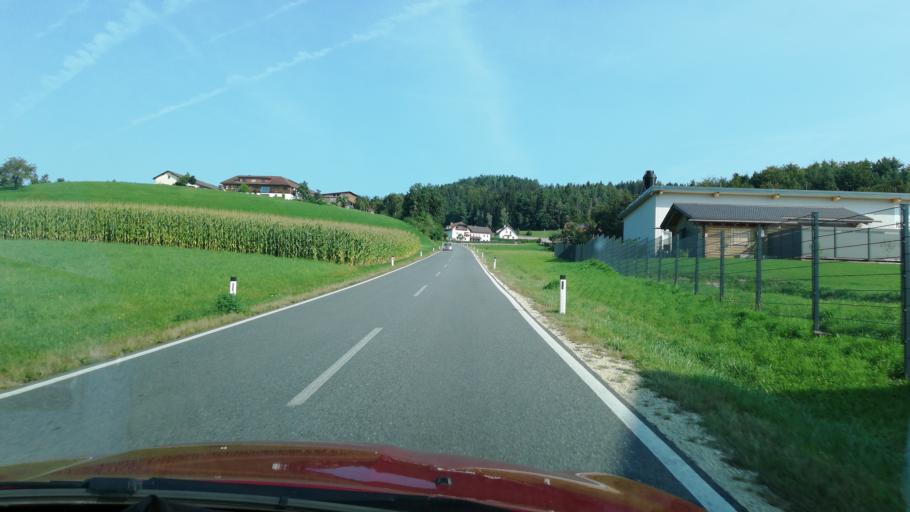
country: AT
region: Upper Austria
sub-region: Politischer Bezirk Perg
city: Perg
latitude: 48.3837
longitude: 14.7069
